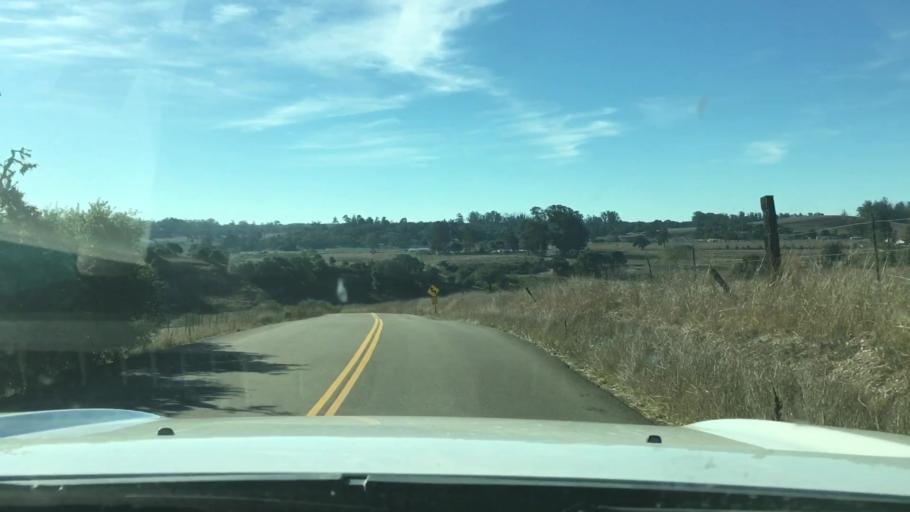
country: US
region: California
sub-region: San Luis Obispo County
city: Arroyo Grande
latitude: 35.0980
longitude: -120.5609
